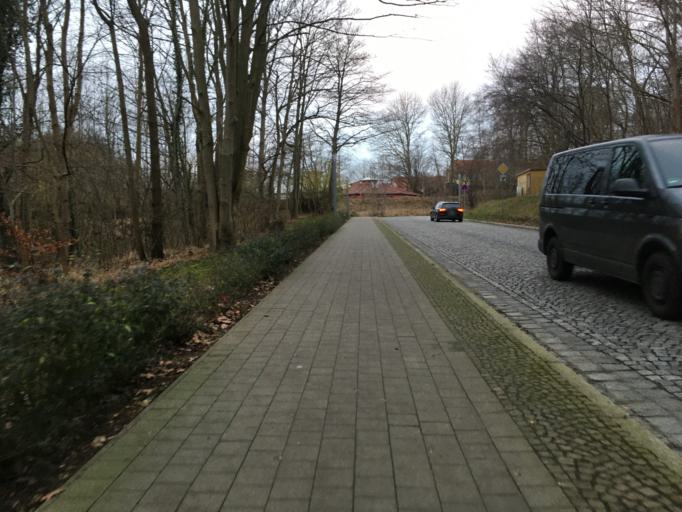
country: DE
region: Mecklenburg-Vorpommern
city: Sassnitz
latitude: 54.5082
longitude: 13.6265
